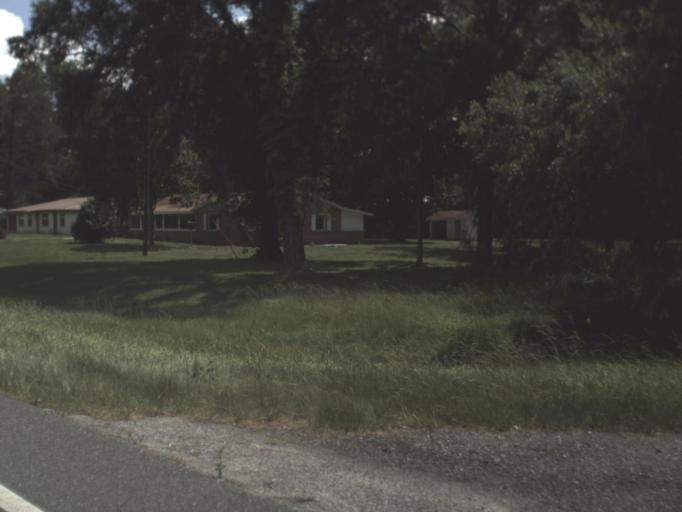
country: US
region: Florida
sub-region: Columbia County
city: Watertown
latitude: 30.0874
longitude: -82.6018
